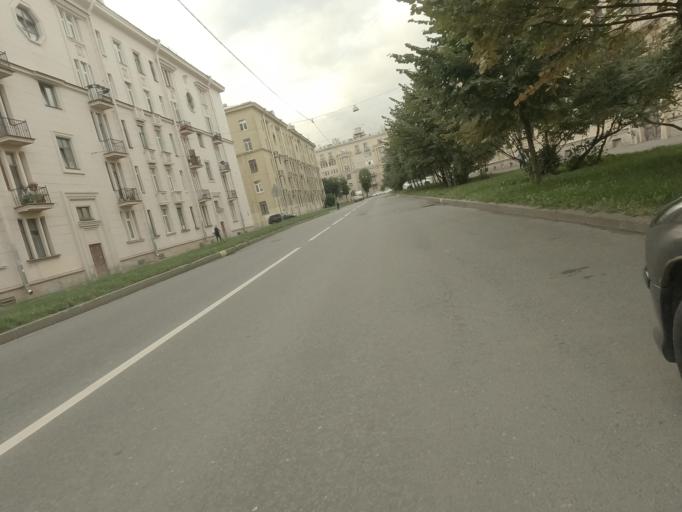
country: RU
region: St.-Petersburg
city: Avtovo
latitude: 59.8695
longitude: 30.2651
